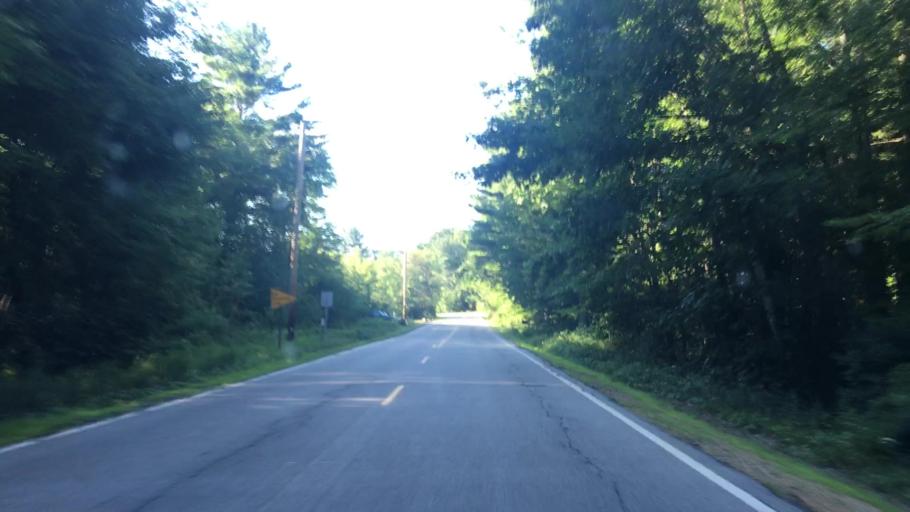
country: US
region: New Hampshire
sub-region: Rockingham County
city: Sandown
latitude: 42.9495
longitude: -71.1955
